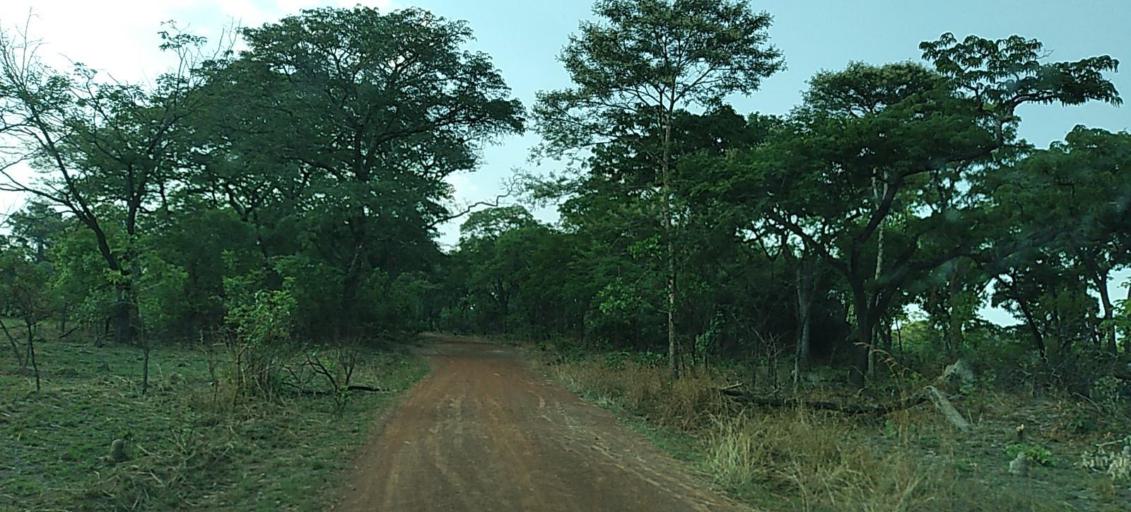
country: ZM
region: Copperbelt
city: Mpongwe
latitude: -13.4345
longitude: 28.0584
